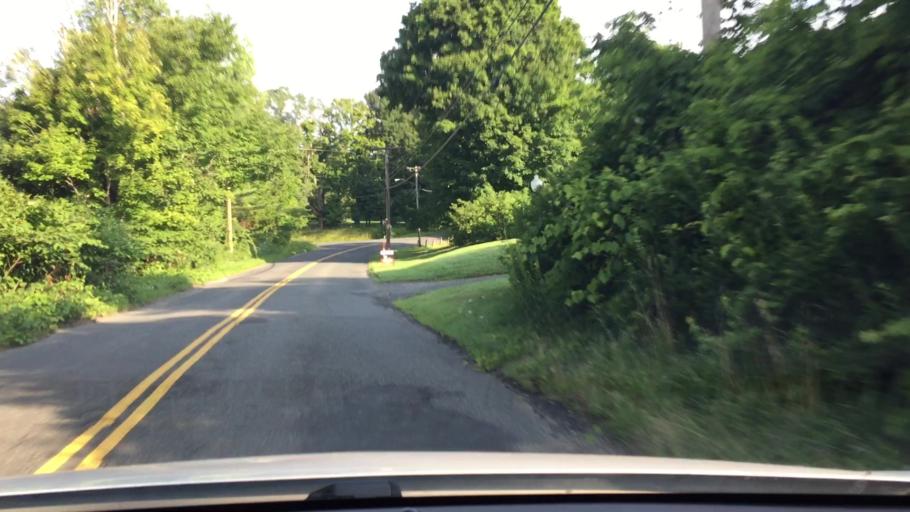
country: US
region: Massachusetts
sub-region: Berkshire County
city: Lee
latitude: 42.3017
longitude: -73.2271
